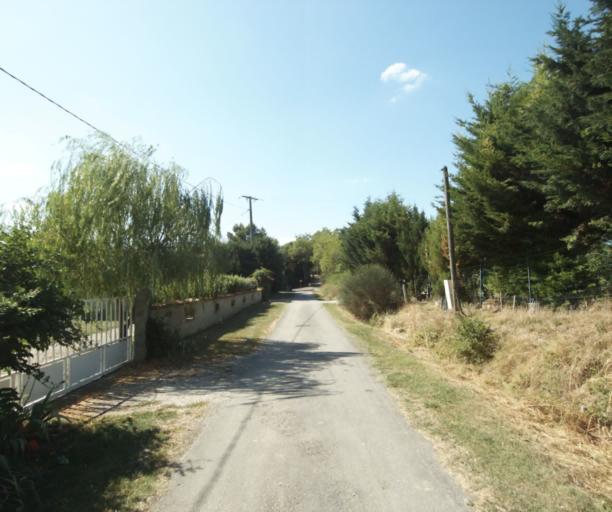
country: FR
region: Midi-Pyrenees
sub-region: Departement de la Haute-Garonne
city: Saint-Felix-Lauragais
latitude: 43.4868
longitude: 1.9020
